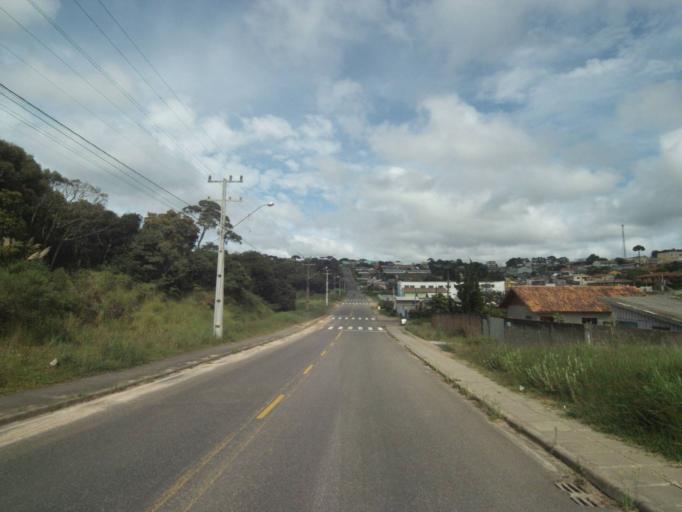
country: BR
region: Parana
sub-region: Quatro Barras
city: Quatro Barras
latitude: -25.3466
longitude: -49.0771
